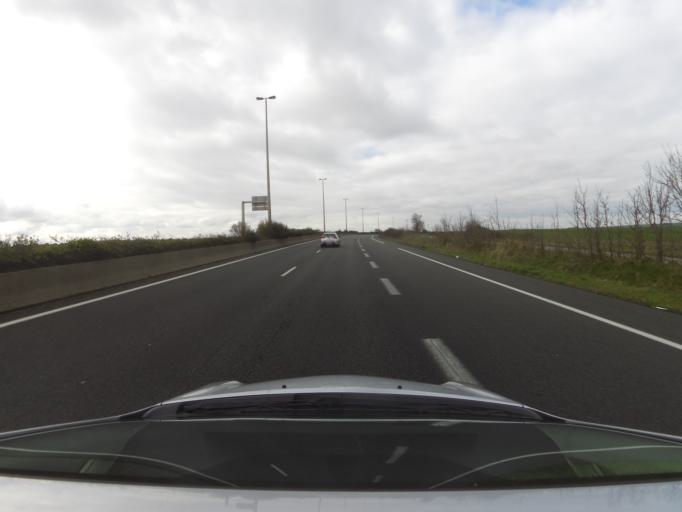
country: FR
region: Nord-Pas-de-Calais
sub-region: Departement du Pas-de-Calais
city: Coquelles
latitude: 50.9110
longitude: 1.7837
